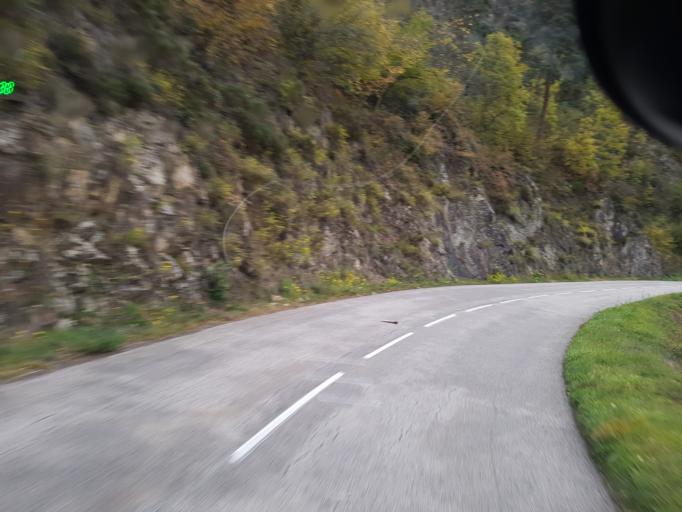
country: FR
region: Auvergne
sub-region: Departement de la Haute-Loire
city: Sainte-Sigolene
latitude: 45.2216
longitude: 4.2066
